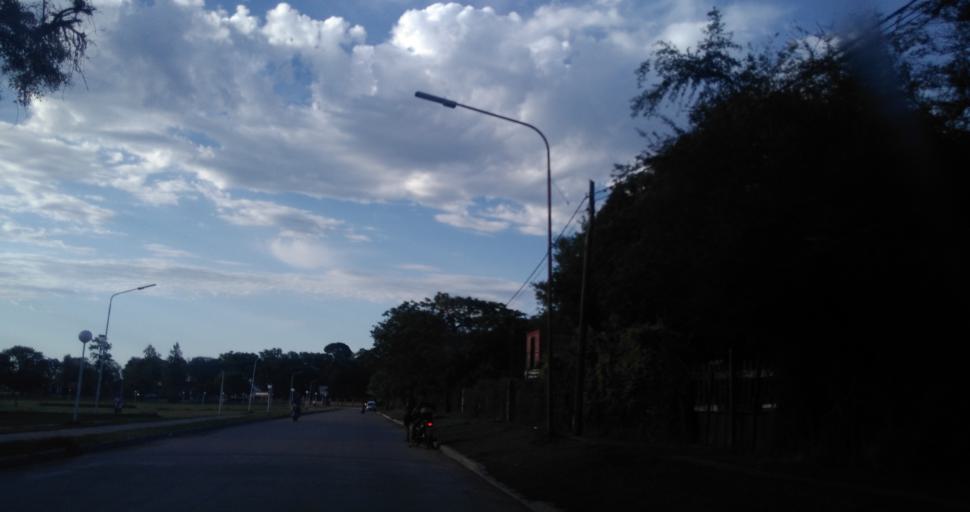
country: AR
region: Chaco
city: Fontana
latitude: -27.4193
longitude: -59.0285
